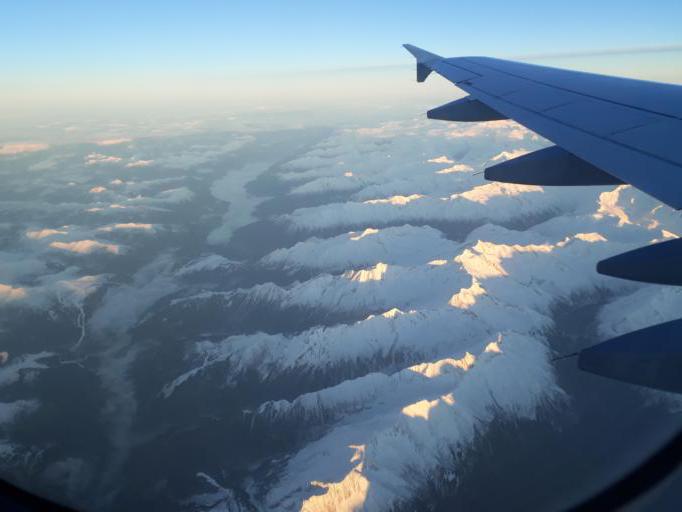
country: AT
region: Tyrol
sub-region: Politischer Bezirk Schwaz
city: Mayrhofen
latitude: 47.1592
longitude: 11.8855
